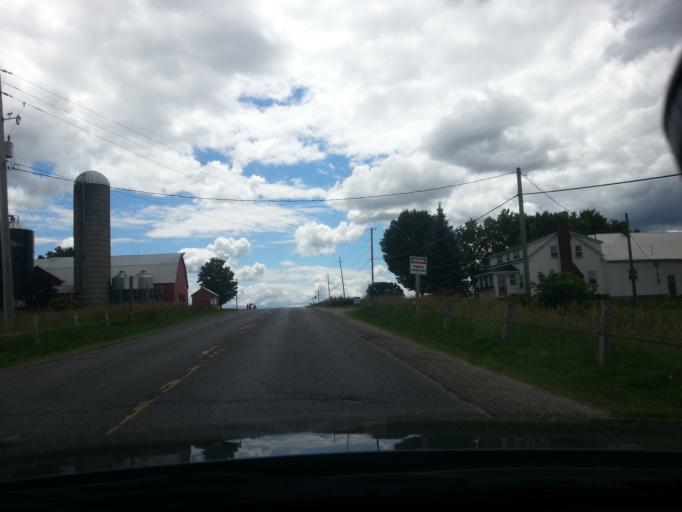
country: CA
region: Ontario
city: Perth
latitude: 44.6212
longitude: -76.2412
